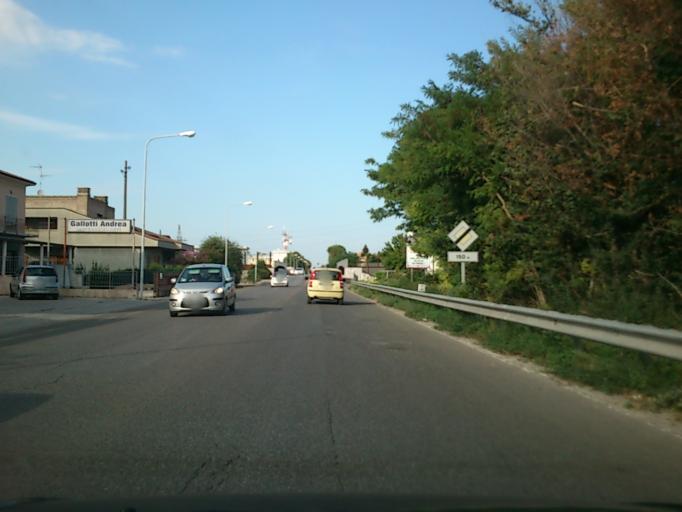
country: IT
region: The Marches
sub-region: Provincia di Pesaro e Urbino
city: Centinarola
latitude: 43.8272
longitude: 12.9950
